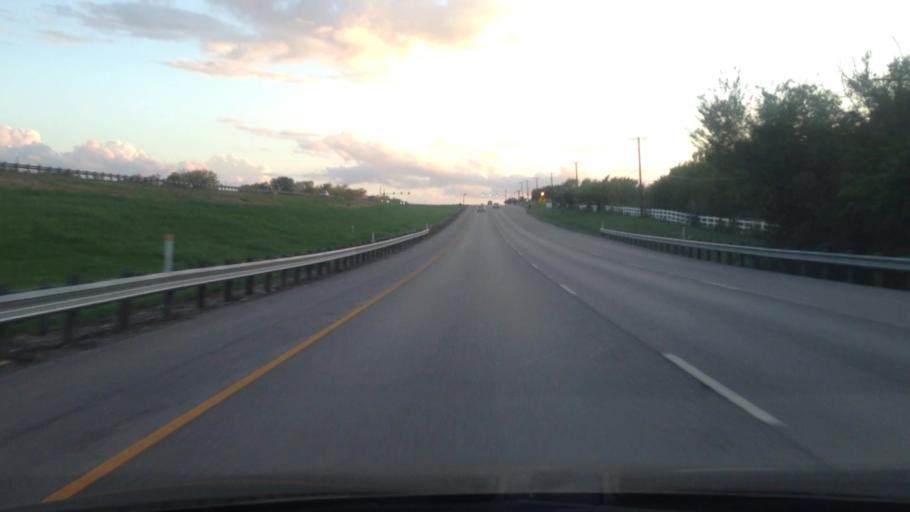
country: US
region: Texas
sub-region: Tarrant County
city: Benbrook
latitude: 32.6533
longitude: -97.4973
